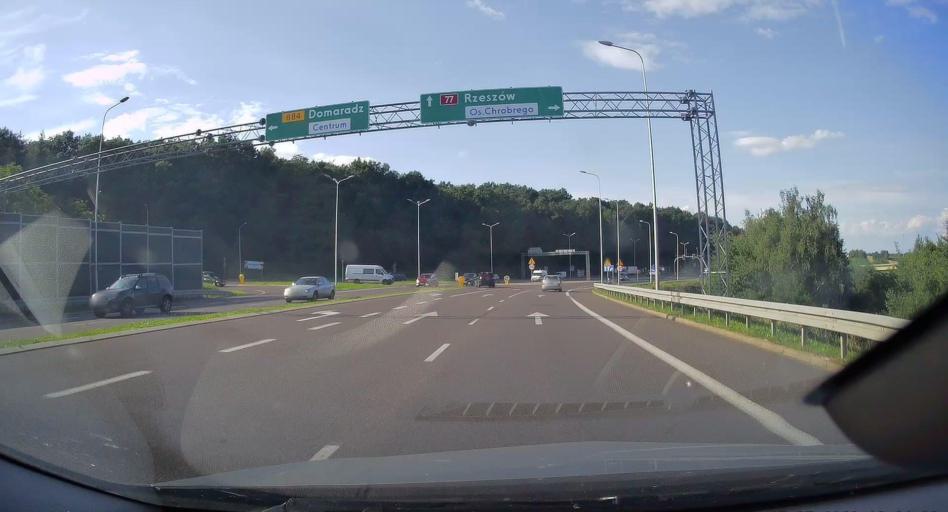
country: PL
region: Subcarpathian Voivodeship
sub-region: Powiat przemyski
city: Zurawica
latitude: 49.8082
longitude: 22.7774
